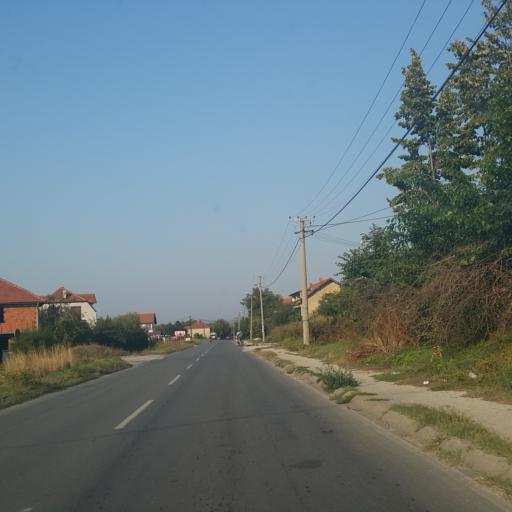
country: RS
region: Central Serbia
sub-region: Zajecarski Okrug
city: Zajecar
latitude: 43.9122
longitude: 22.2676
